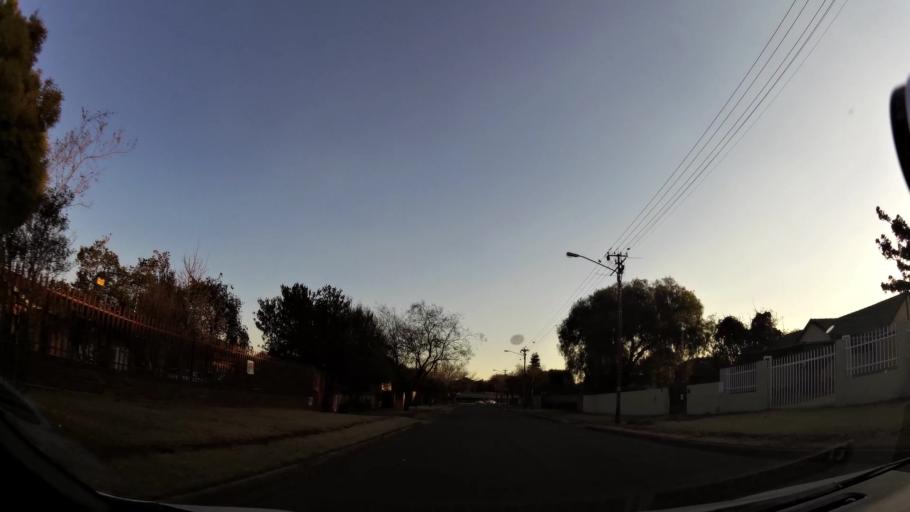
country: ZA
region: Gauteng
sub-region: Ekurhuleni Metropolitan Municipality
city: Germiston
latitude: -26.2545
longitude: 28.1737
